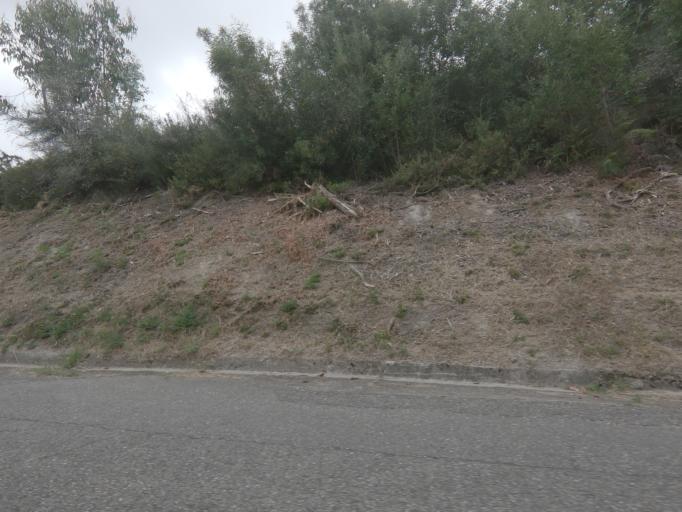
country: ES
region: Galicia
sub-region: Provincia de Pontevedra
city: Tui
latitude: 42.0479
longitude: -8.6571
